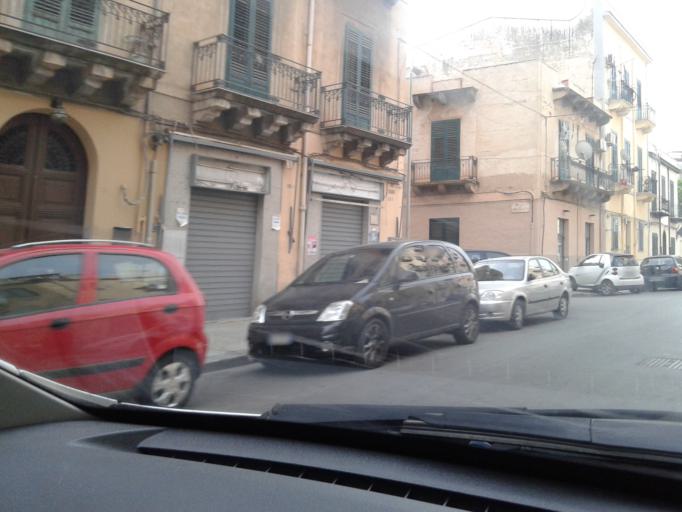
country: IT
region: Sicily
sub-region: Palermo
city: Palermo
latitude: 38.1058
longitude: 13.3410
